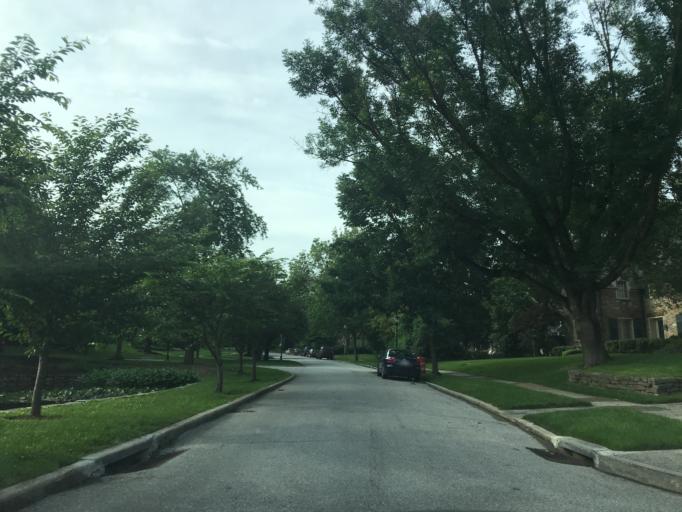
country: US
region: Maryland
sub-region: Baltimore County
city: Towson
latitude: 39.3585
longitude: -76.6161
